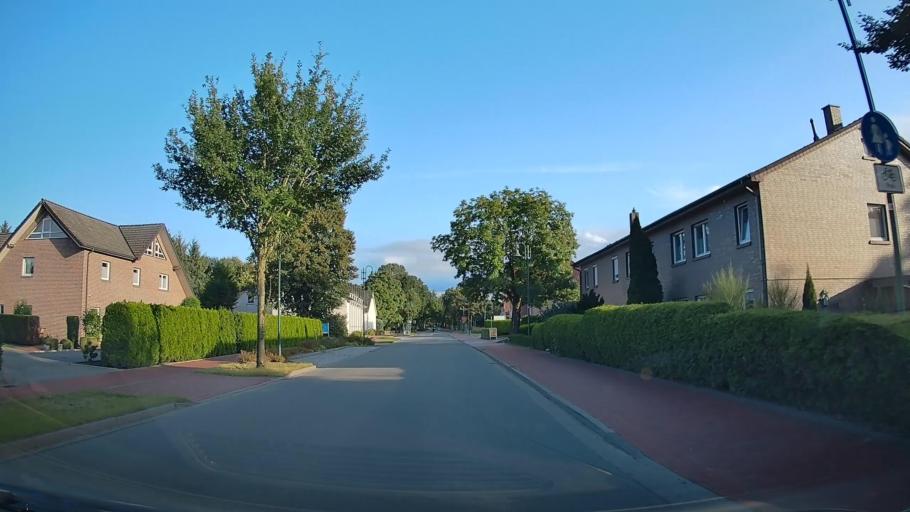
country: DE
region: Lower Saxony
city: Hilkenbrook
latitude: 53.0393
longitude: 7.7414
